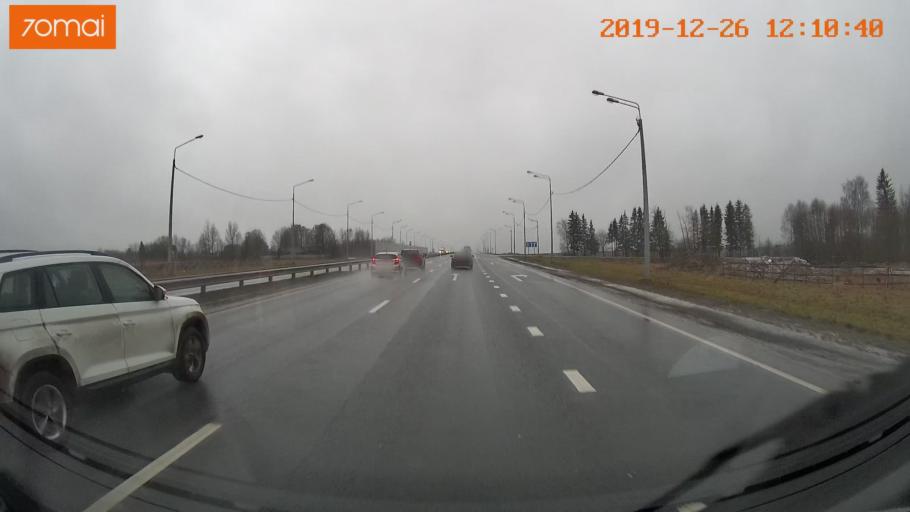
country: RU
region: Vologda
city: Tonshalovo
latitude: 59.2573
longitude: 37.9772
